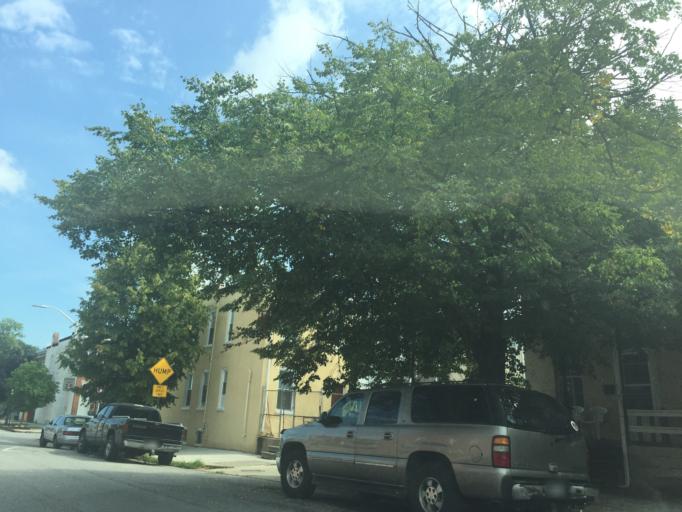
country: US
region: Maryland
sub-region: City of Baltimore
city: Baltimore
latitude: 39.3196
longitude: -76.6112
